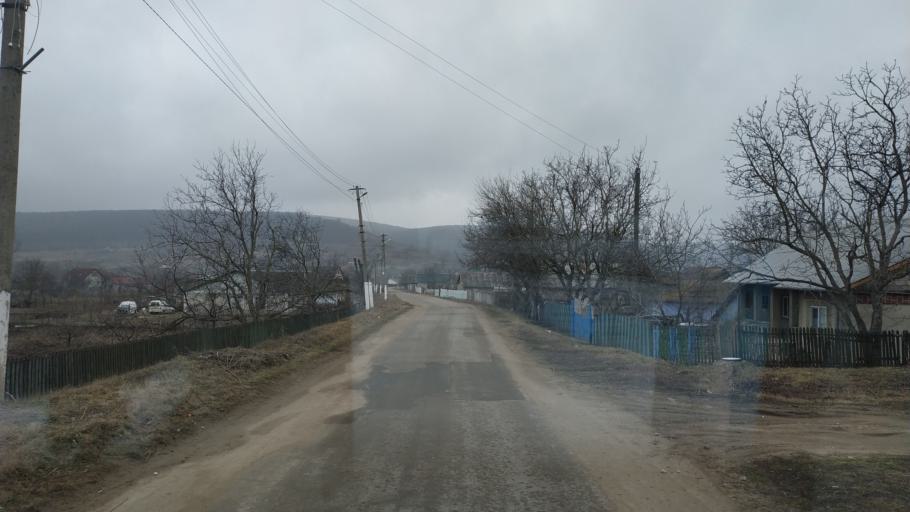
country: MD
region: Hincesti
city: Hincesti
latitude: 46.9592
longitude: 28.4983
